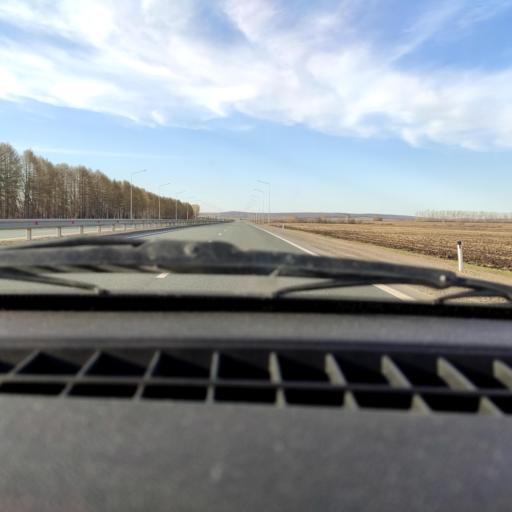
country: RU
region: Bashkortostan
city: Sterlitamak
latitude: 53.7625
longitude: 55.9446
